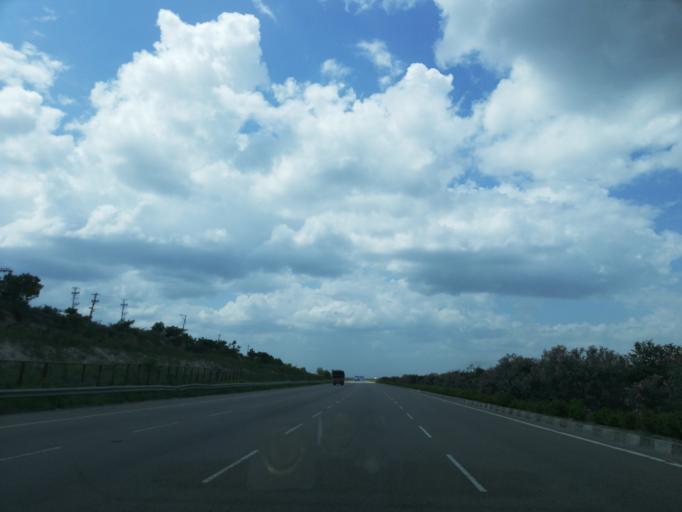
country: IN
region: Telangana
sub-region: Medak
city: Serilingampalle
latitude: 17.4324
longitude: 78.2626
